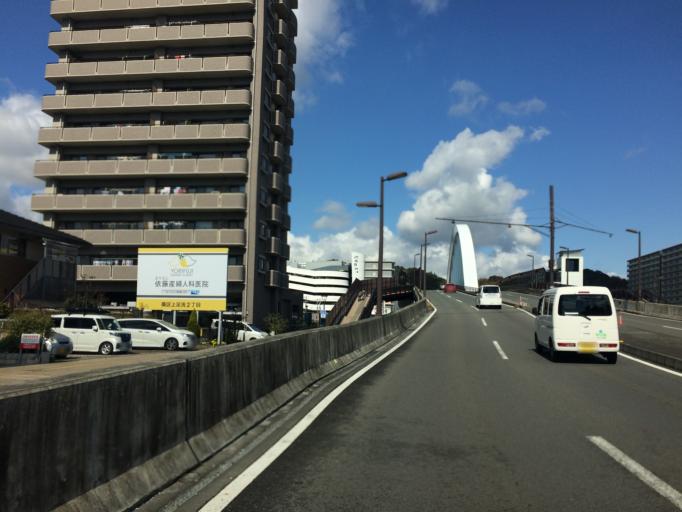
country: JP
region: Shizuoka
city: Shizuoka-shi
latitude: 34.9825
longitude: 138.4127
